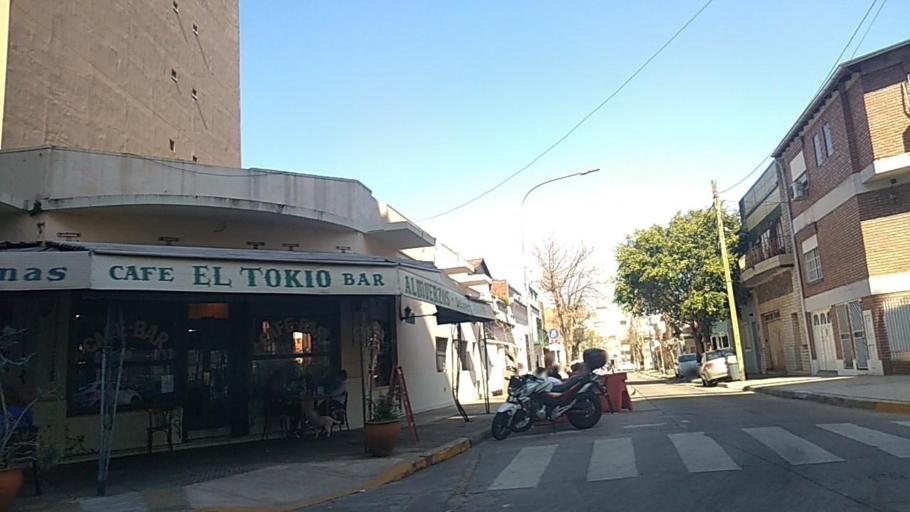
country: AR
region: Buenos Aires F.D.
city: Villa Santa Rita
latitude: -34.6124
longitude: -58.4916
